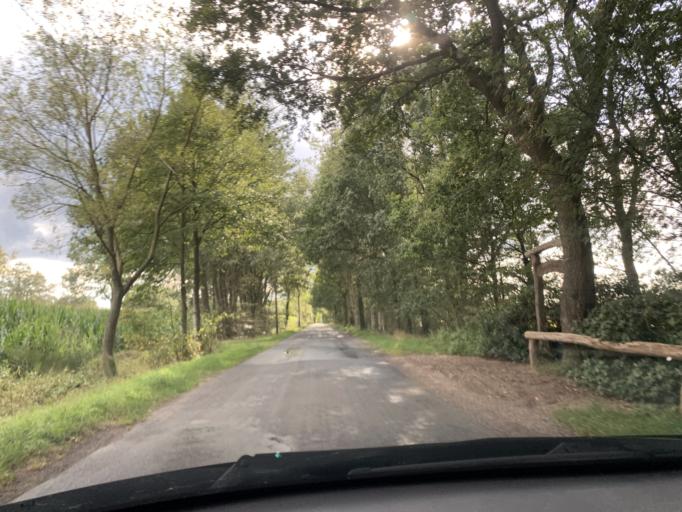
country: DE
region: Lower Saxony
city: Westerstede
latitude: 53.3127
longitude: 7.9853
